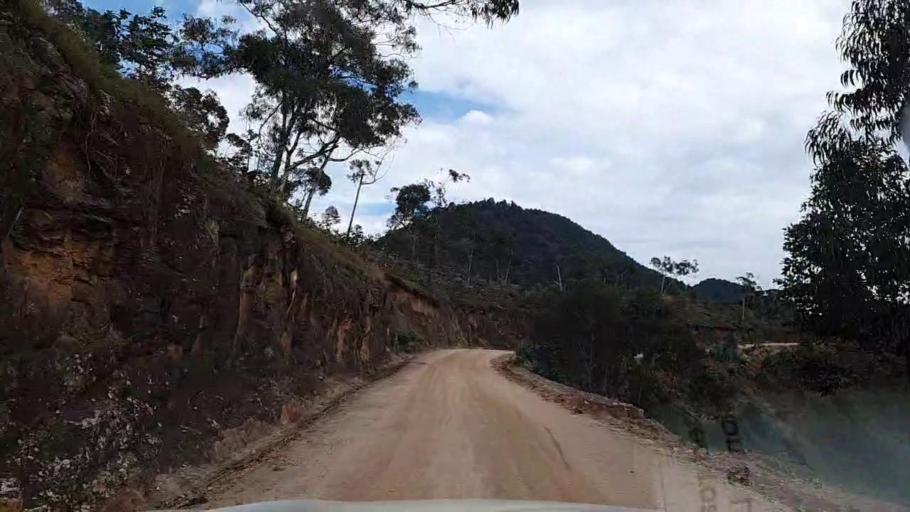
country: RW
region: Southern Province
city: Nzega
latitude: -2.3907
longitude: 29.4516
